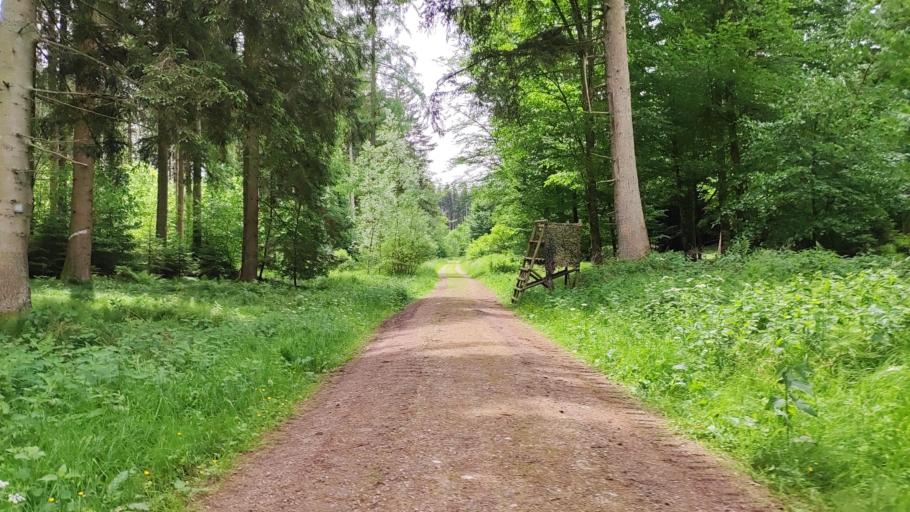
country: DE
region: Bavaria
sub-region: Swabia
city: Landensberg
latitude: 48.4254
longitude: 10.5032
